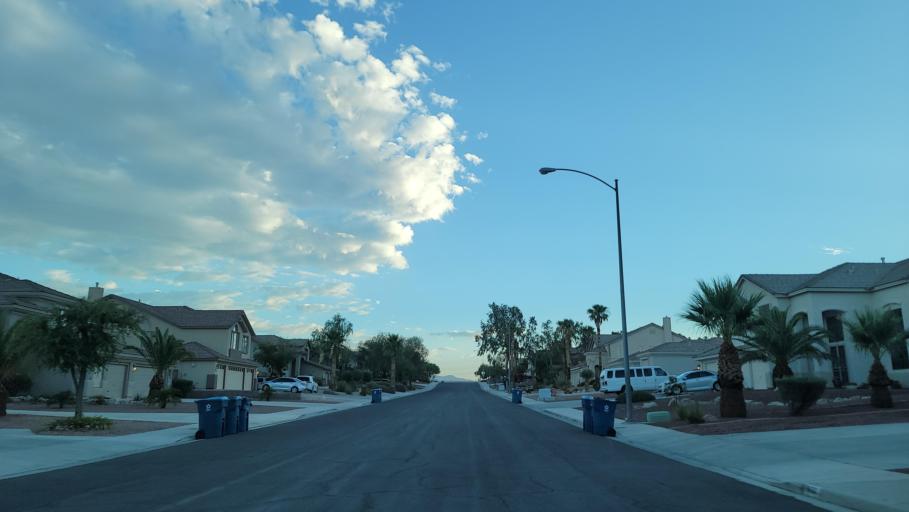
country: US
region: Nevada
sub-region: Clark County
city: Sunrise Manor
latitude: 36.1785
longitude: -115.0205
